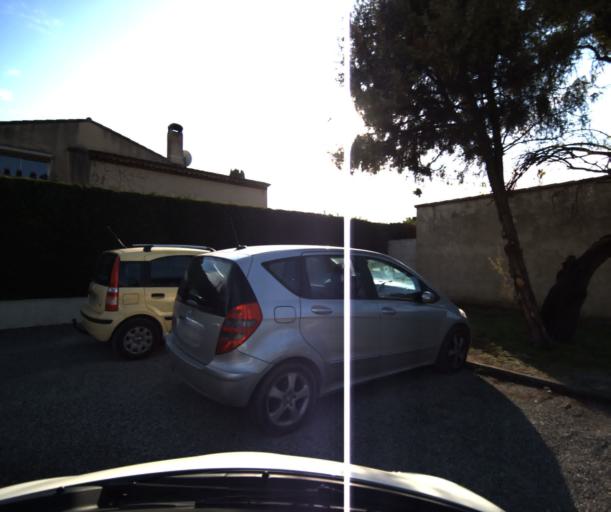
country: FR
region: Provence-Alpes-Cote d'Azur
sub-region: Departement du Vaucluse
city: Pertuis
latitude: 43.6924
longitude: 5.5197
